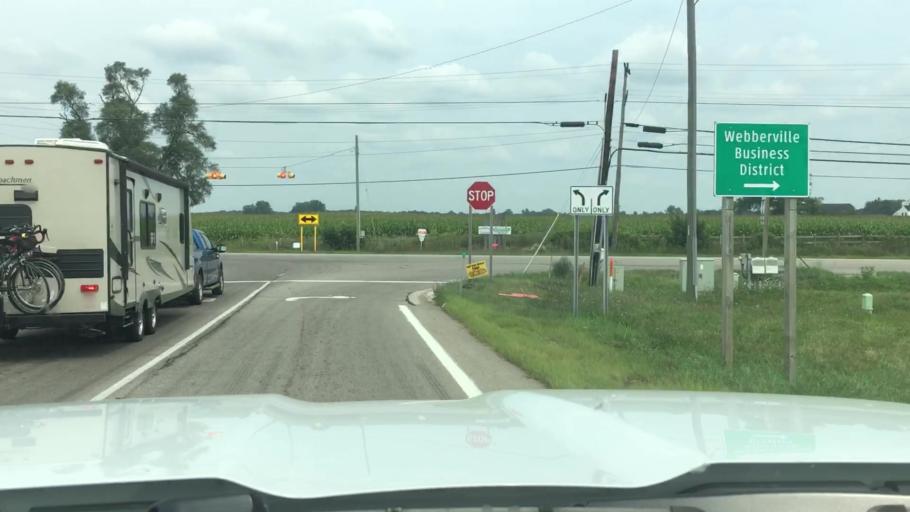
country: US
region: Michigan
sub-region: Ingham County
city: Webberville
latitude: 42.6689
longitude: -84.1986
